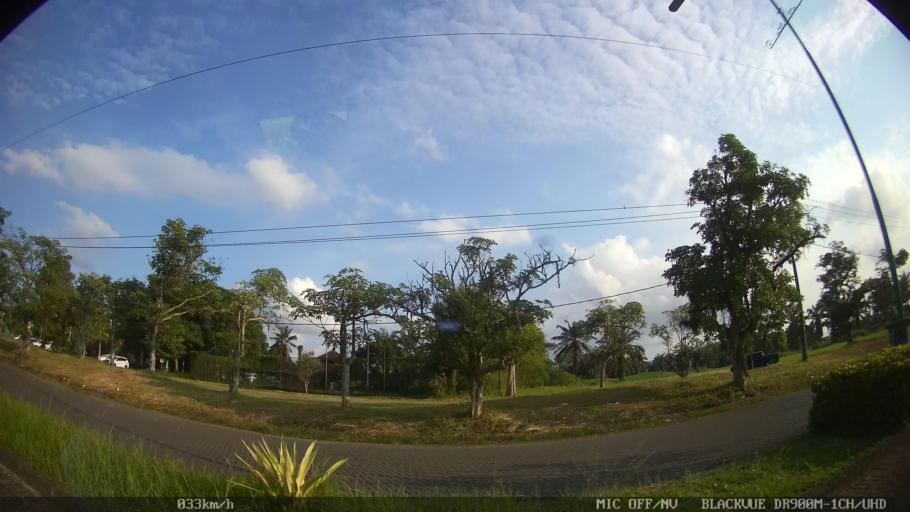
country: ID
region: North Sumatra
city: Medan
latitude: 3.6257
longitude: 98.6457
